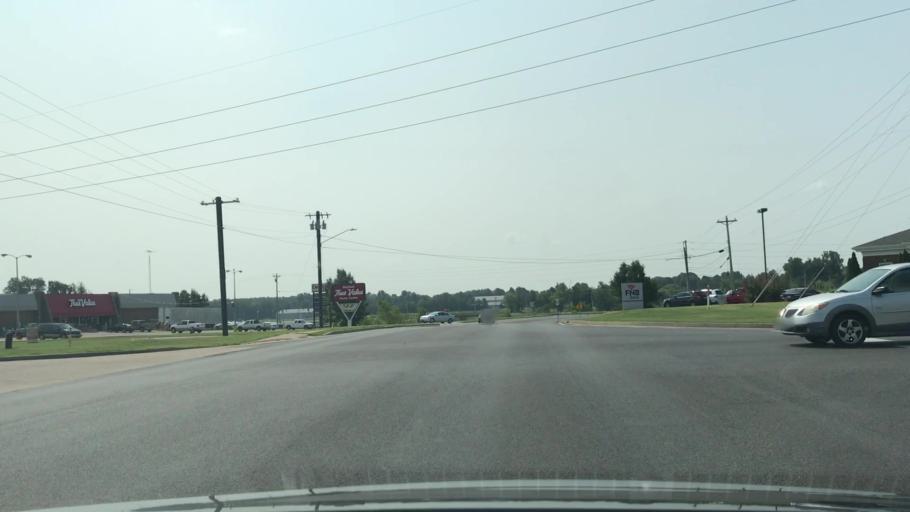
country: US
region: Kentucky
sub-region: Graves County
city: Mayfield
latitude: 36.7191
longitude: -88.6255
